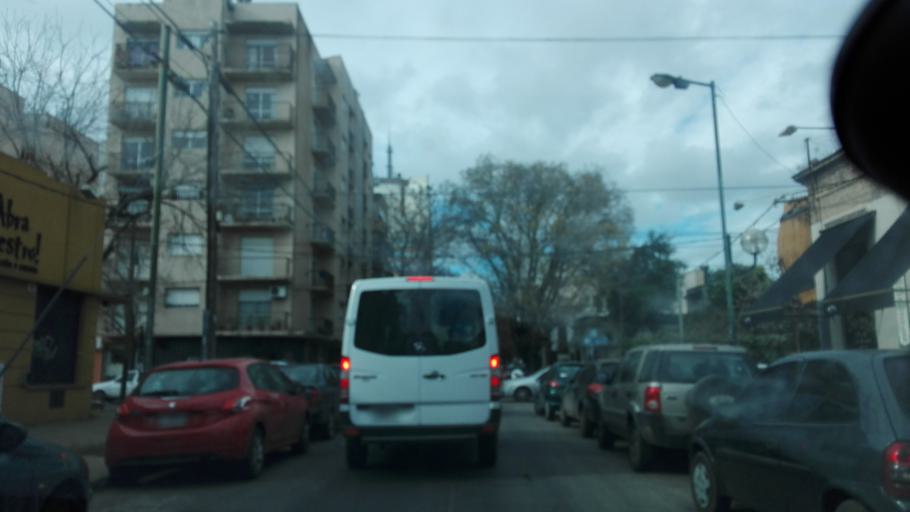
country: AR
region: Buenos Aires
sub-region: Partido de La Plata
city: La Plata
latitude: -34.9154
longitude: -57.9651
